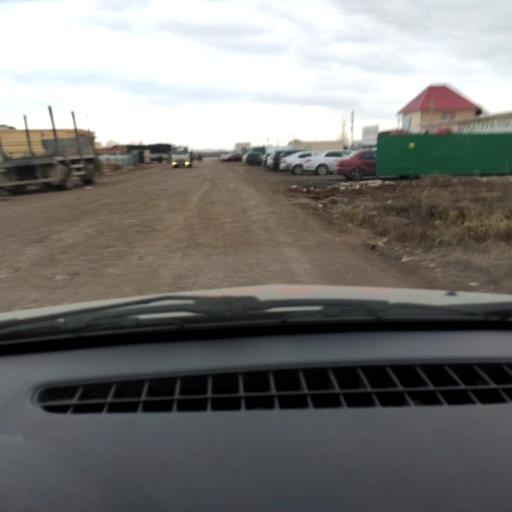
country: RU
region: Bashkortostan
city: Ufa
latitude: 54.6167
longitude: 55.8929
